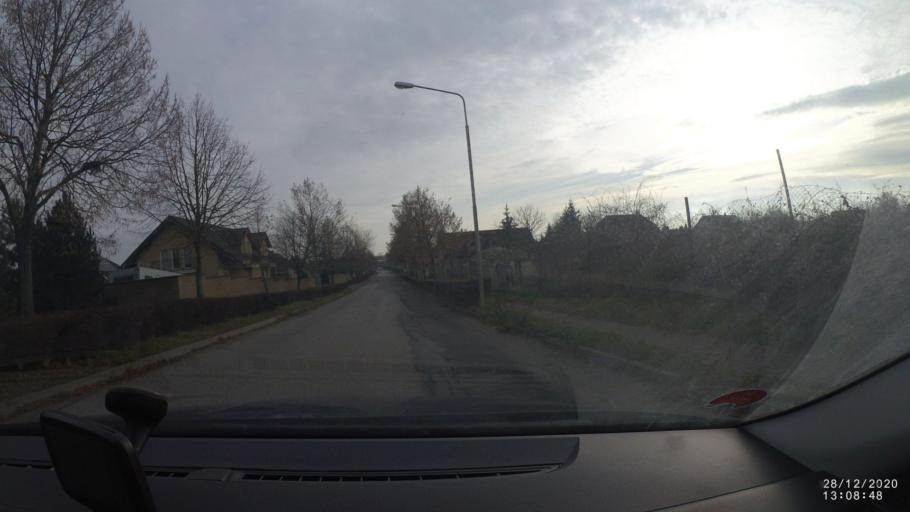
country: CZ
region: Central Bohemia
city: Zelenec
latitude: 50.1298
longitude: 14.6649
